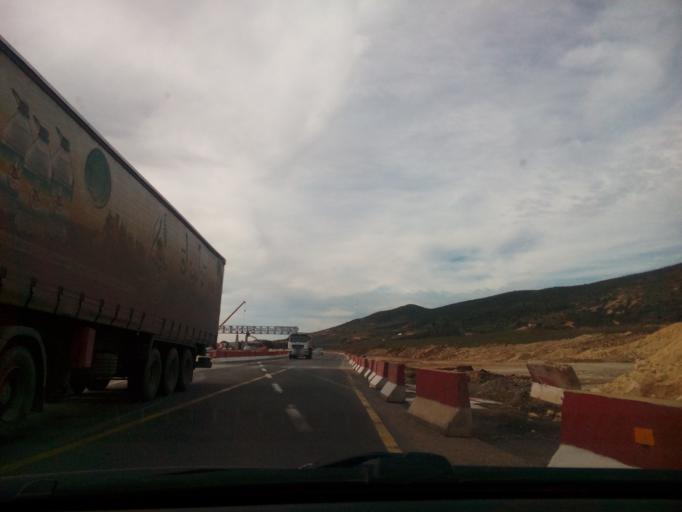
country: DZ
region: Sidi Bel Abbes
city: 'Ain el Berd
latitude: 35.3849
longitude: -0.4949
